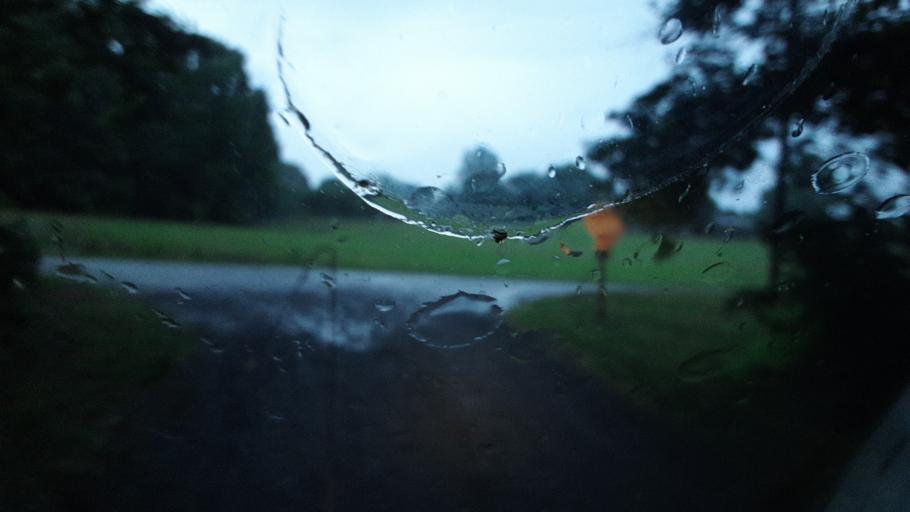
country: US
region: North Carolina
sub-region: Yadkin County
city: Jonesville
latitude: 36.0769
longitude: -80.8559
